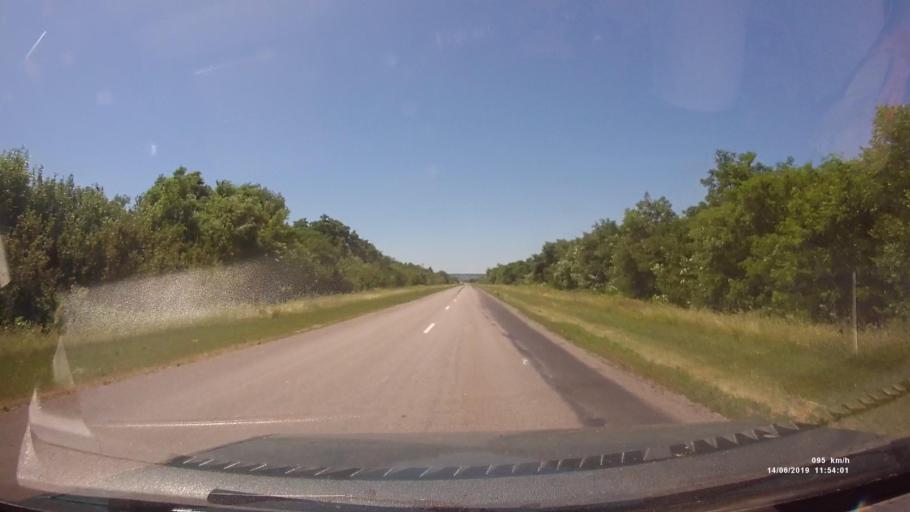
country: RU
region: Rostov
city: Kazanskaya
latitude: 49.8225
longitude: 41.2019
